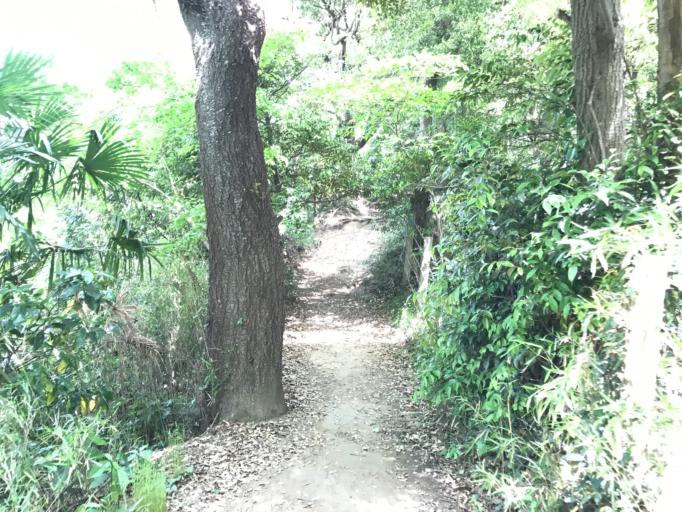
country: JP
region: Kanagawa
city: Kamakura
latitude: 35.3191
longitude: 139.5335
